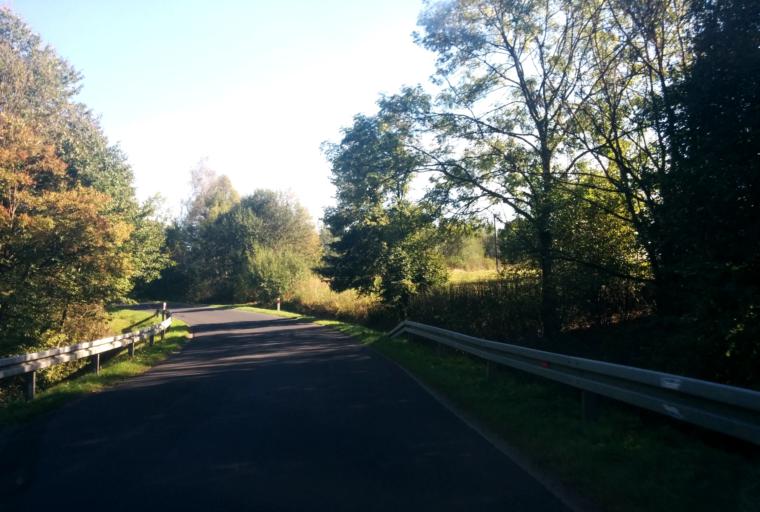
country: PL
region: Subcarpathian Voivodeship
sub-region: Powiat leski
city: Polanczyk
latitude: 49.3390
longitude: 22.4179
